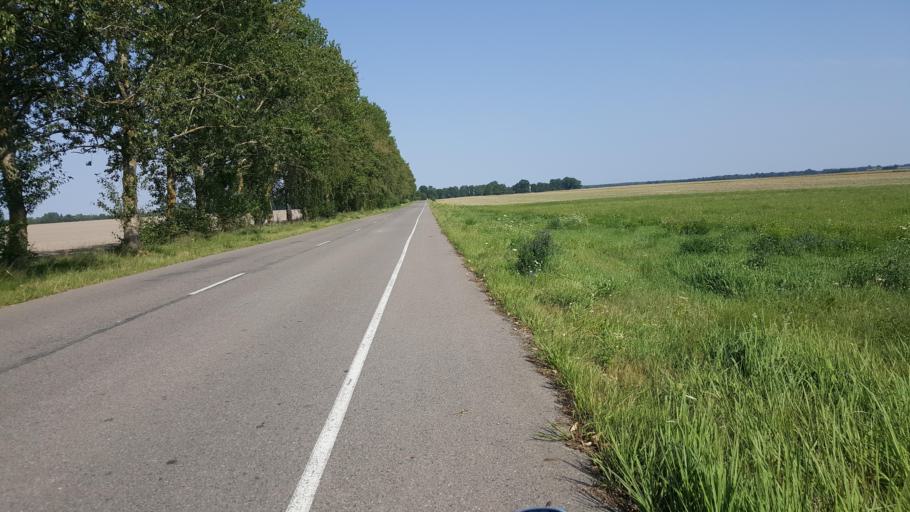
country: BY
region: Brest
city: Zhabinka
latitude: 52.2371
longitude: 23.9880
